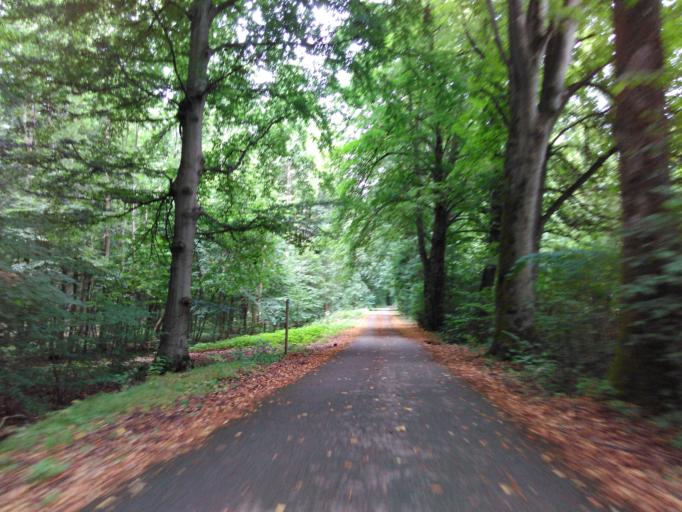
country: LU
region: Luxembourg
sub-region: Canton de Luxembourg
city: Sandweiler
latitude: 49.6455
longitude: 6.2171
